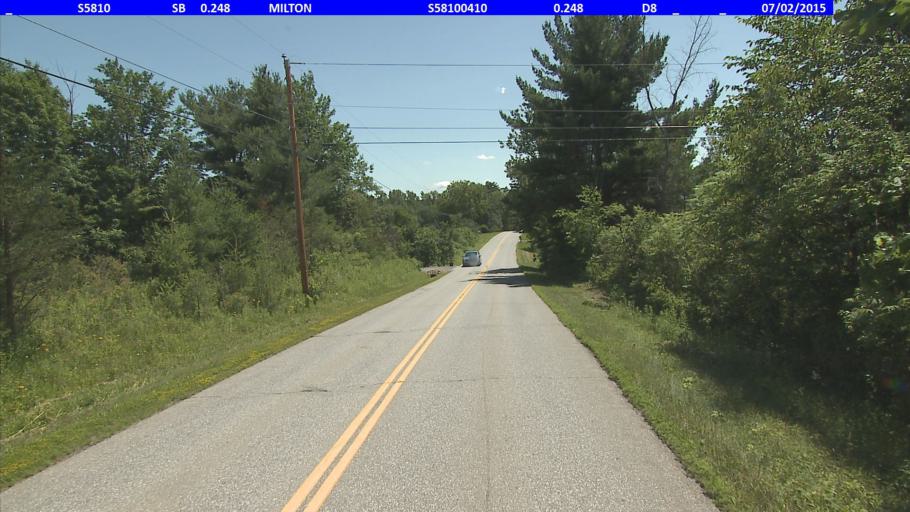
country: US
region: Vermont
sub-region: Chittenden County
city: Colchester
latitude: 44.5854
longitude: -73.1295
